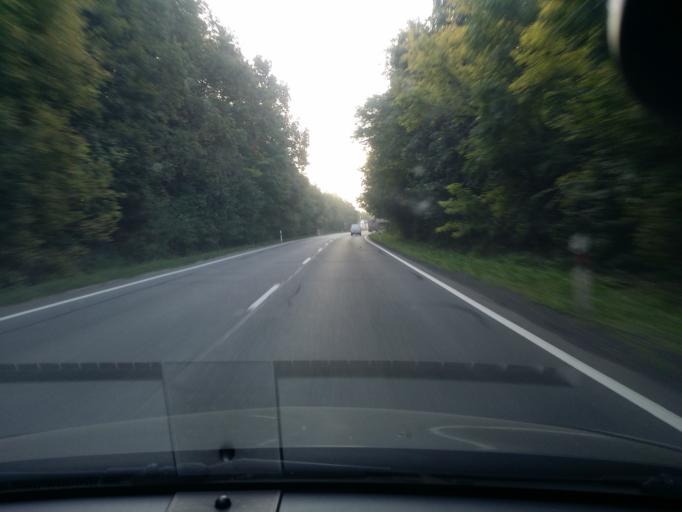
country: HU
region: Fejer
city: Dunaujvaros
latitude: 46.9303
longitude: 18.9282
